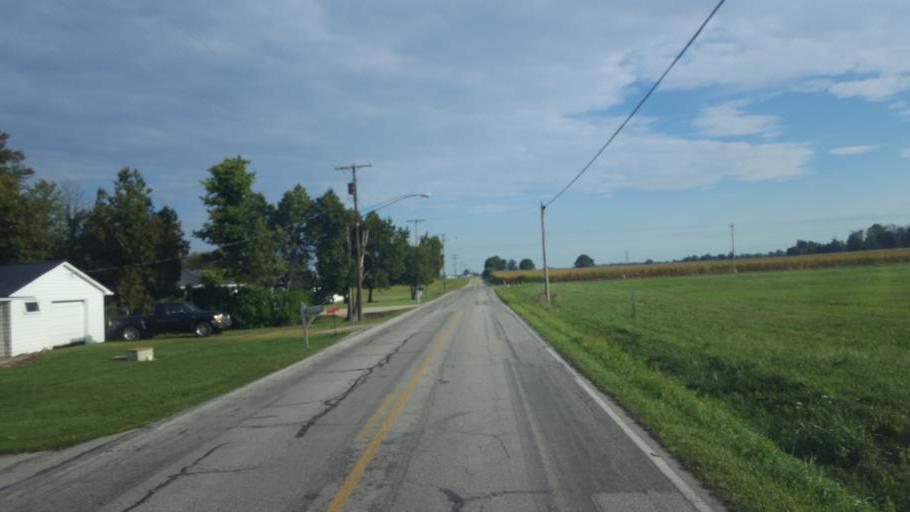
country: US
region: Ohio
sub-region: Crawford County
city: Galion
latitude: 40.6741
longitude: -82.9098
